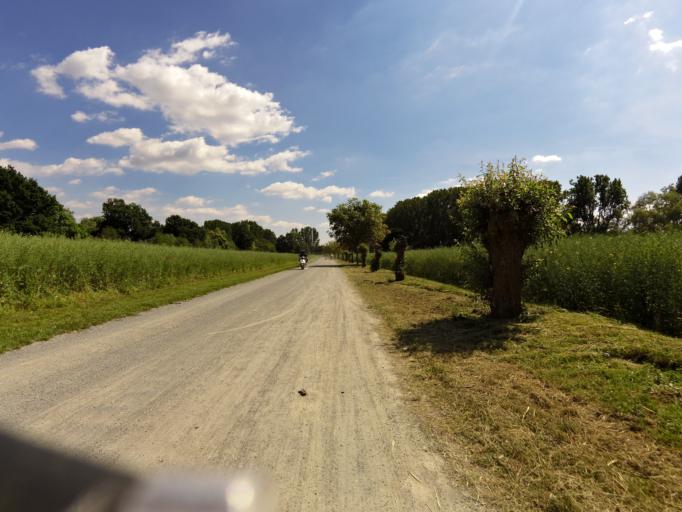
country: DE
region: Rheinland-Pfalz
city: Nackenheim
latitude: 49.9385
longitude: 8.3499
